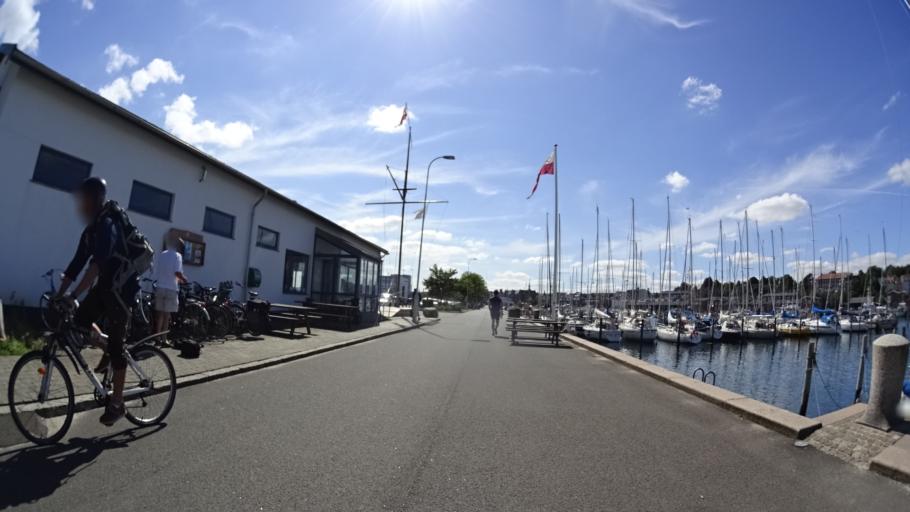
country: DK
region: Central Jutland
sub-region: Arhus Kommune
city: Arhus
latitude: 56.1656
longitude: 10.2228
